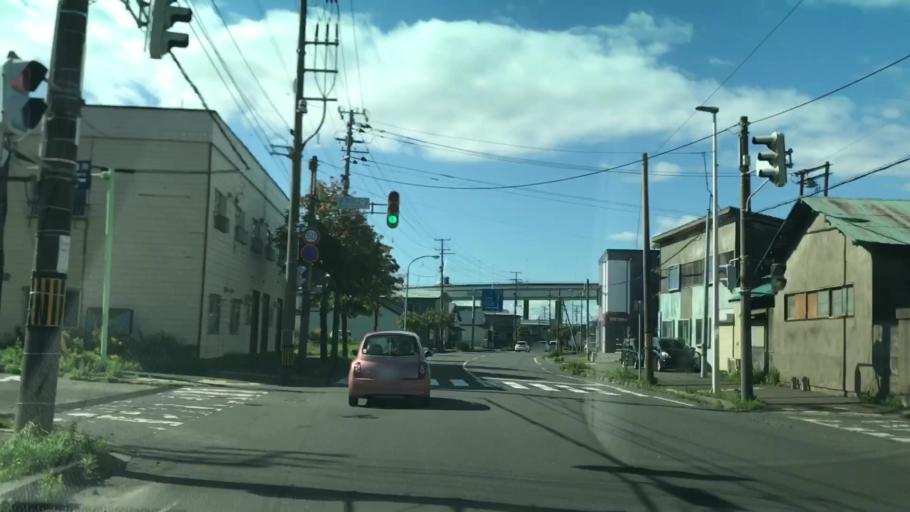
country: JP
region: Hokkaido
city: Muroran
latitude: 42.3395
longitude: 140.9524
